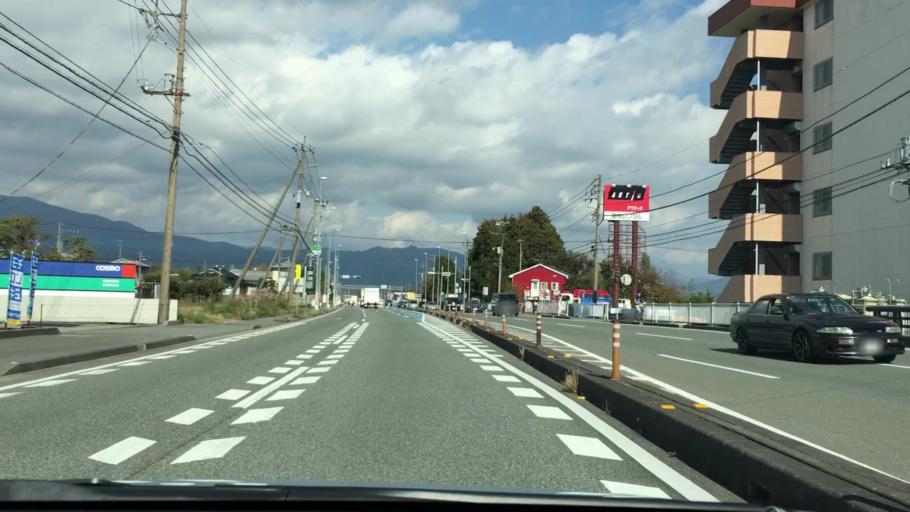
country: JP
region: Shizuoka
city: Gotemba
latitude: 35.3174
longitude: 138.9299
